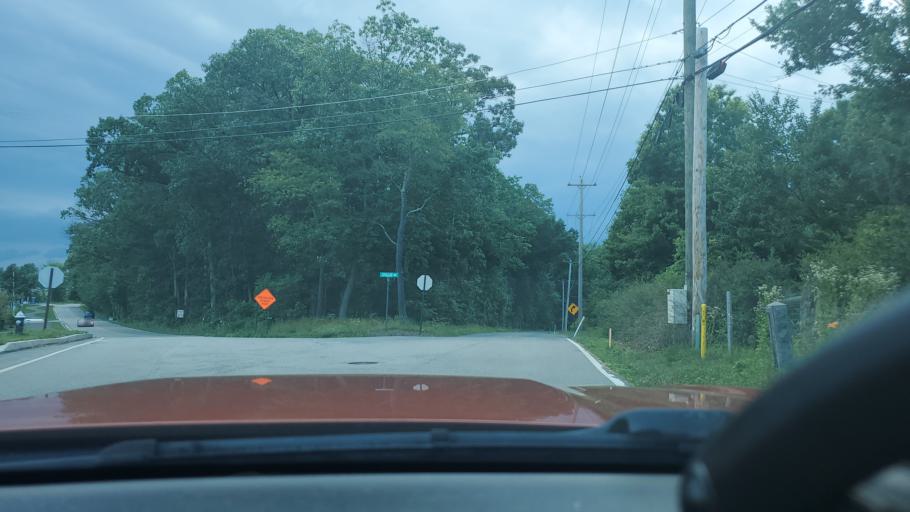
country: US
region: Pennsylvania
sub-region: Montgomery County
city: Limerick
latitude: 40.2416
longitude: -75.5197
